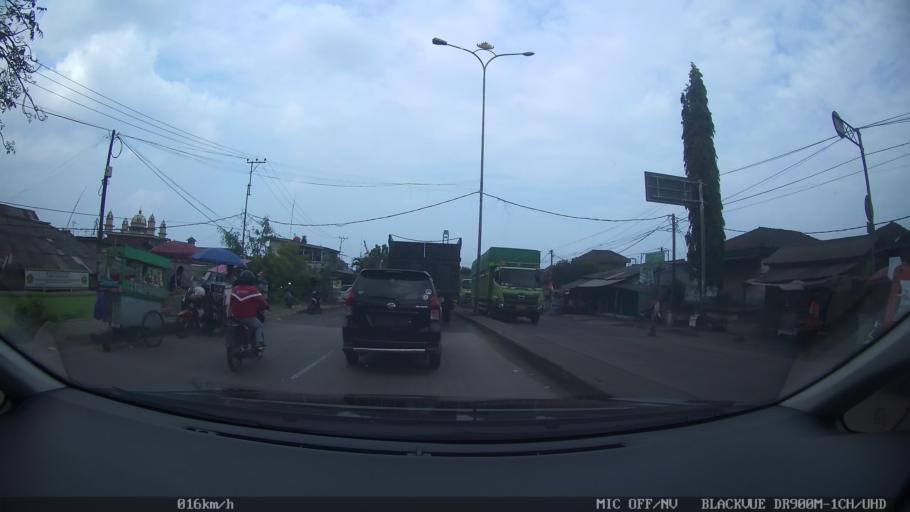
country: ID
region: Lampung
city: Panjang
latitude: -5.4628
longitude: 105.3205
